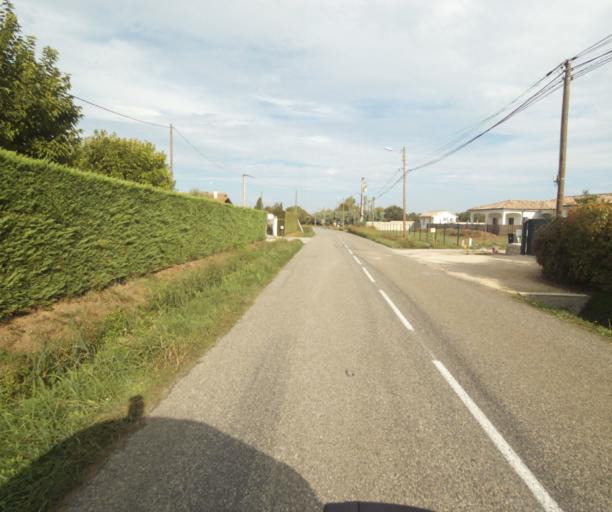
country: FR
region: Midi-Pyrenees
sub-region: Departement du Tarn-et-Garonne
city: Montech
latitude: 43.9654
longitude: 1.2344
